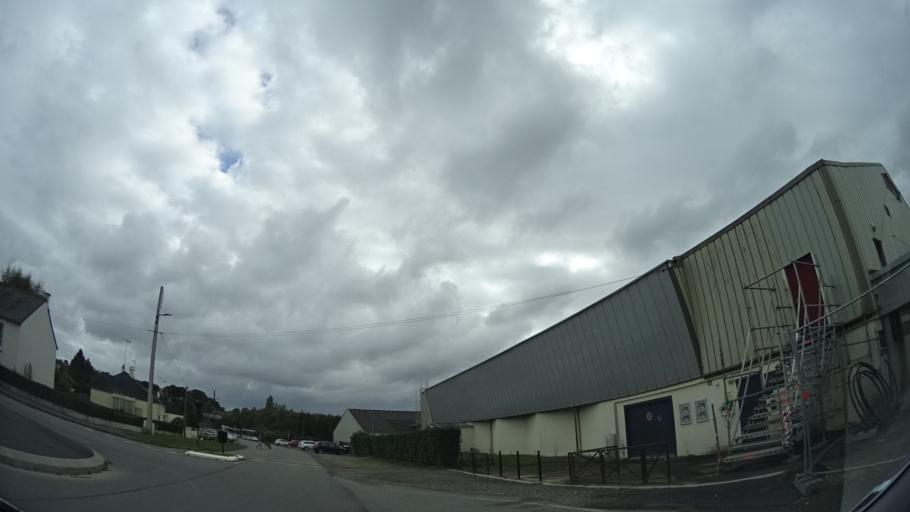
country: FR
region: Brittany
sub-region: Departement d'Ille-et-Vilaine
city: Chasne-sur-Illet
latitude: 48.2590
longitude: -1.6031
